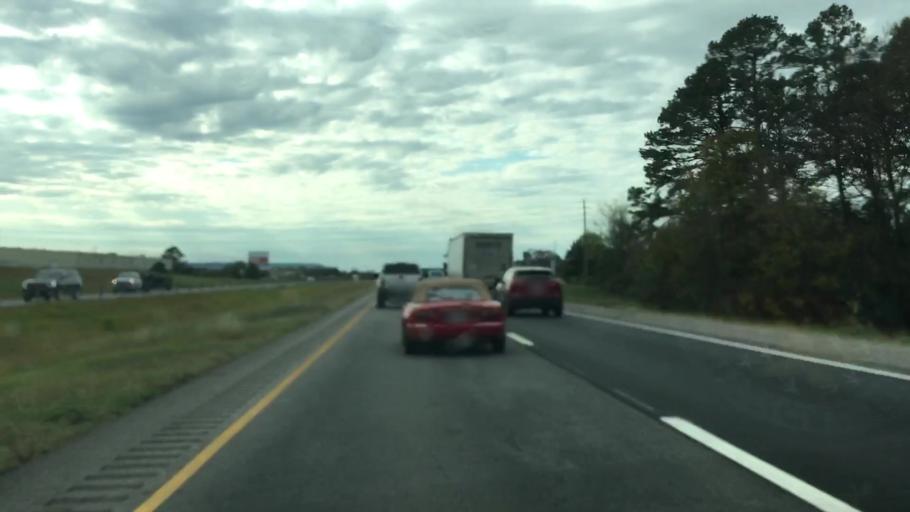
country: US
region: Arkansas
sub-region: Conway County
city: Morrilton
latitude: 35.1742
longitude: -92.7079
